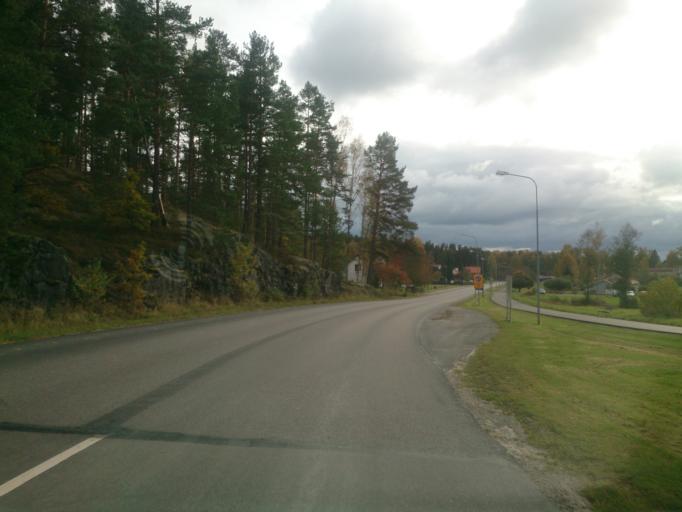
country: SE
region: OEstergoetland
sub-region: Atvidabergs Kommun
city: Atvidaberg
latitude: 58.2115
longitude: 16.0123
